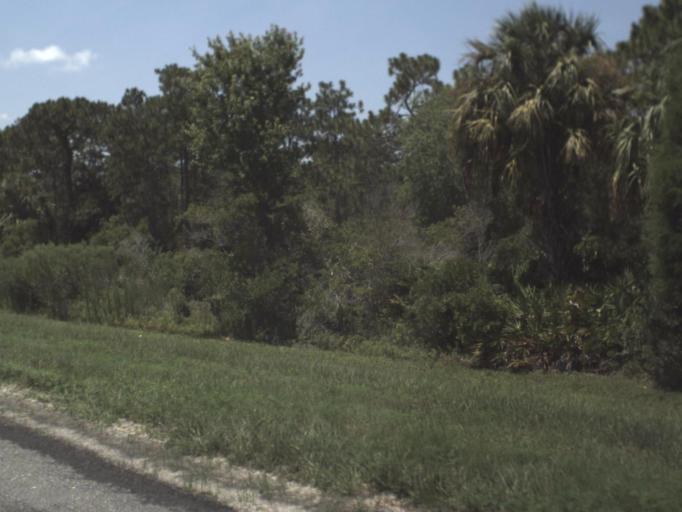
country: US
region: Florida
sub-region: Citrus County
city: Sugarmill Woods
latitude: 28.6889
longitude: -82.5526
